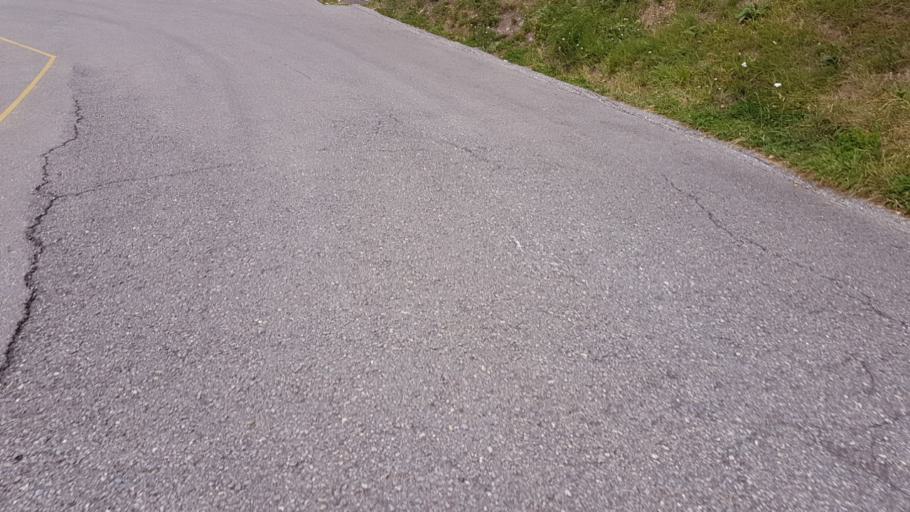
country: CH
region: Valais
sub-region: Leuk District
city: Leukerbad
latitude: 46.3836
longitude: 7.6248
